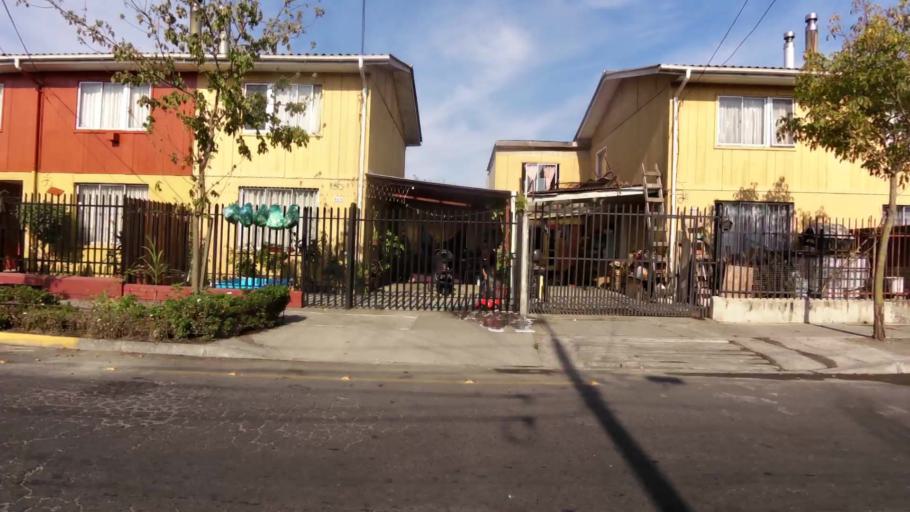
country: CL
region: Biobio
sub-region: Provincia de Concepcion
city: Talcahuano
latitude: -36.7963
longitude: -73.1143
